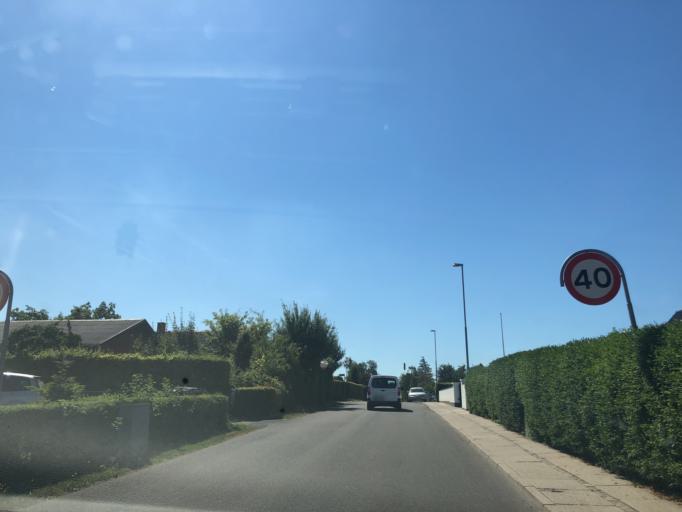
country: DK
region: Zealand
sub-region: Slagelse Kommune
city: Forlev
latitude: 55.3685
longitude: 11.2602
